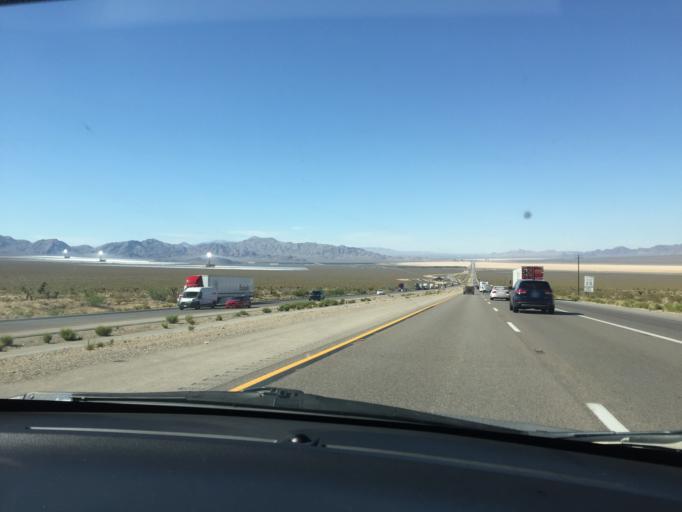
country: US
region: Nevada
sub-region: Clark County
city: Sandy Valley
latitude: 35.4822
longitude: -115.4447
